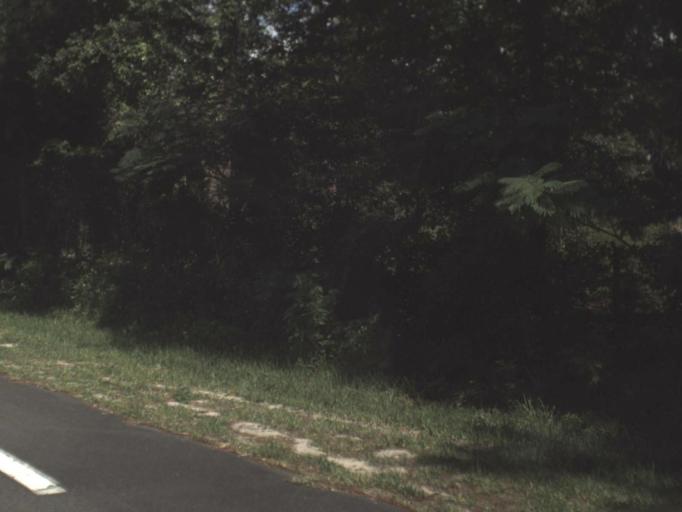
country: US
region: Florida
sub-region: Clay County
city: Keystone Heights
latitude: 29.7125
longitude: -82.0284
